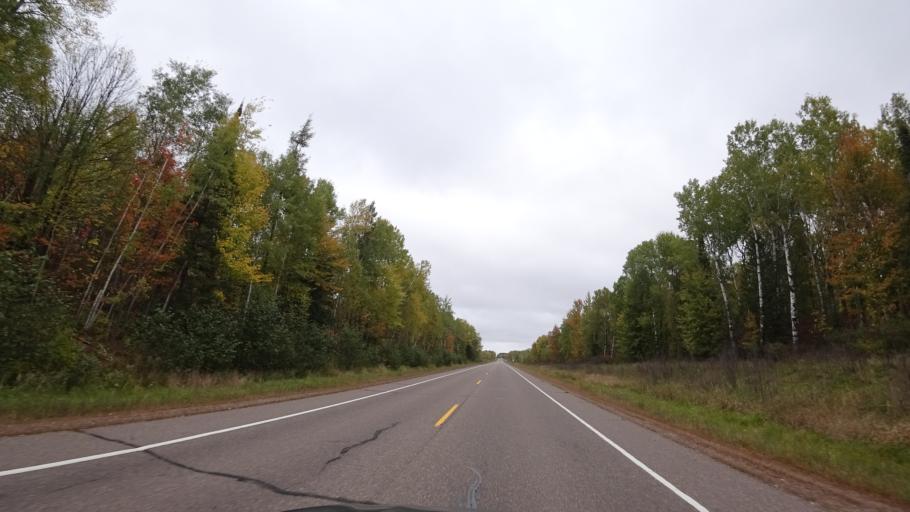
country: US
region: Wisconsin
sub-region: Rusk County
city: Ladysmith
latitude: 45.5622
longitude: -91.1117
